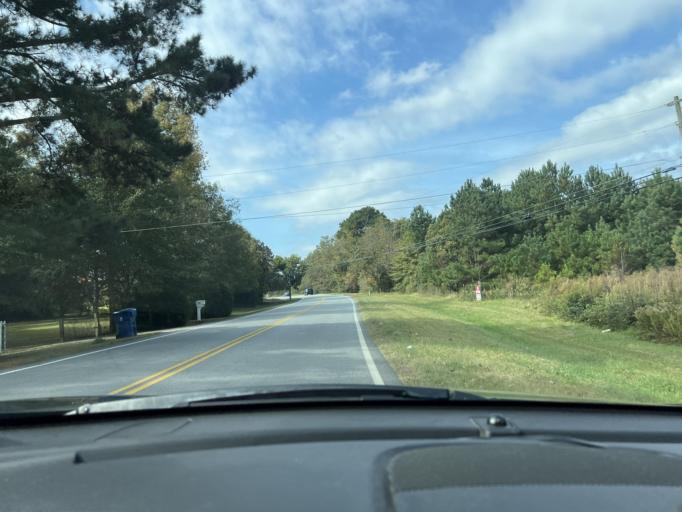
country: US
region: Georgia
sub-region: Gwinnett County
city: Grayson
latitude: 33.9020
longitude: -83.9756
